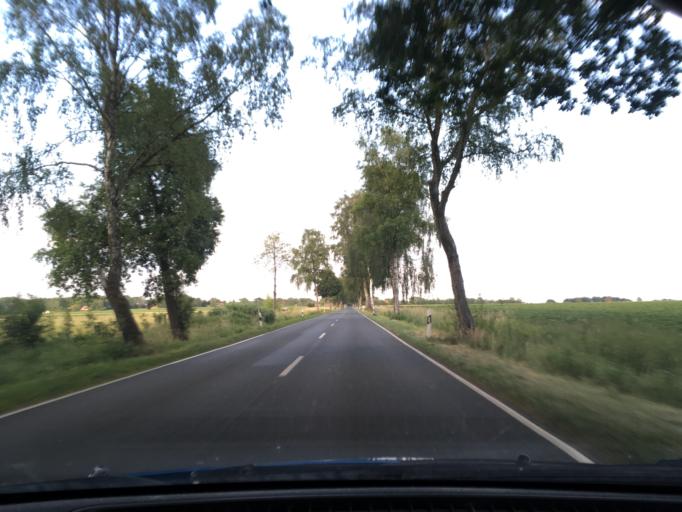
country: DE
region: Lower Saxony
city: Scharnhorst
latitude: 52.7218
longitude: 10.2996
